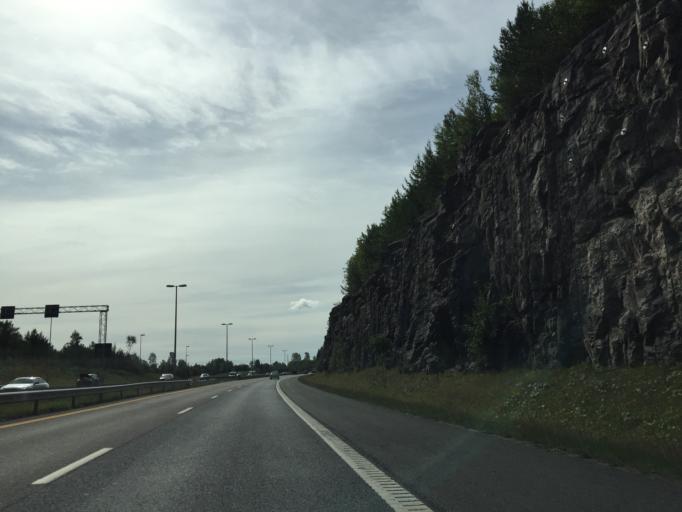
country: NO
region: Akershus
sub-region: As
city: As
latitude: 59.6884
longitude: 10.7355
